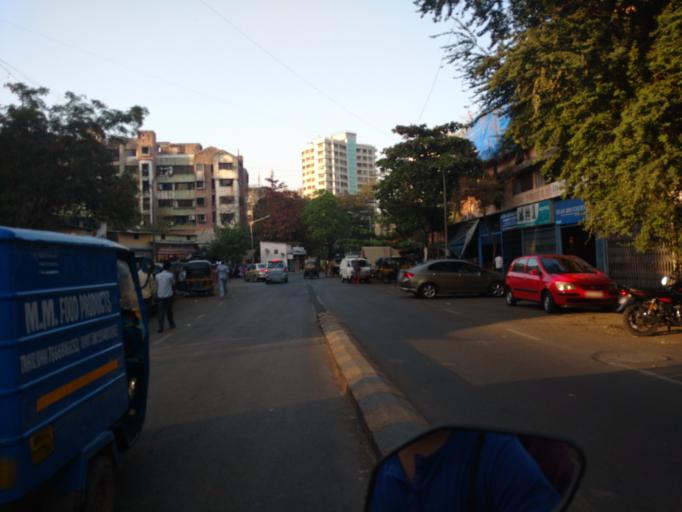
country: IN
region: Maharashtra
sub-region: Mumbai Suburban
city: Borivli
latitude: 19.2044
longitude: 72.8378
